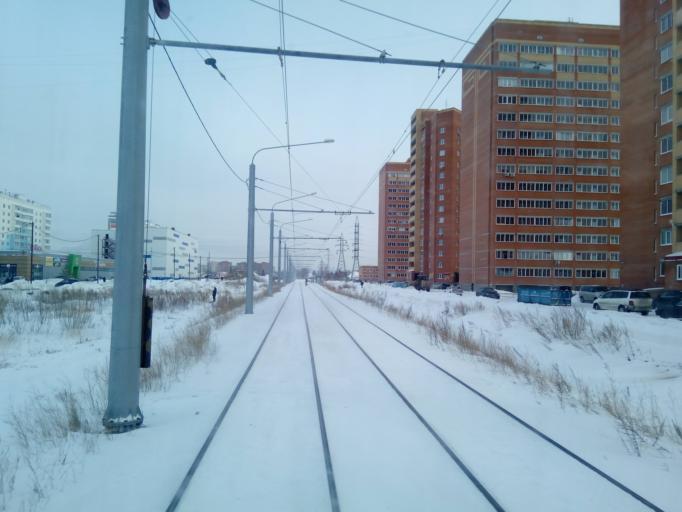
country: RU
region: Novosibirsk
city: Tolmachevo
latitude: 54.9789
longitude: 82.8084
